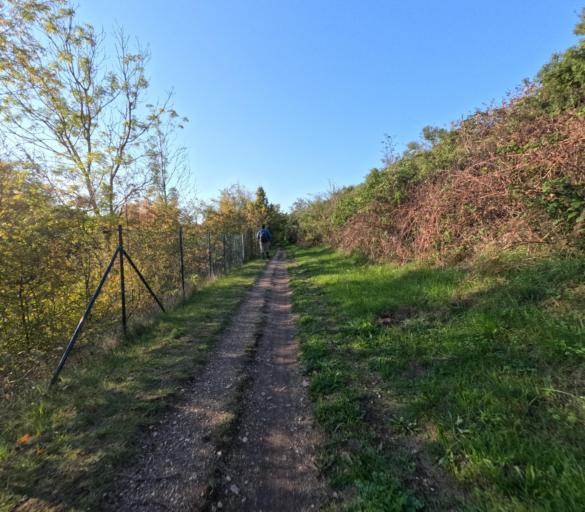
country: DE
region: Saxony
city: Markranstadt
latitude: 51.3408
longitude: 12.2891
